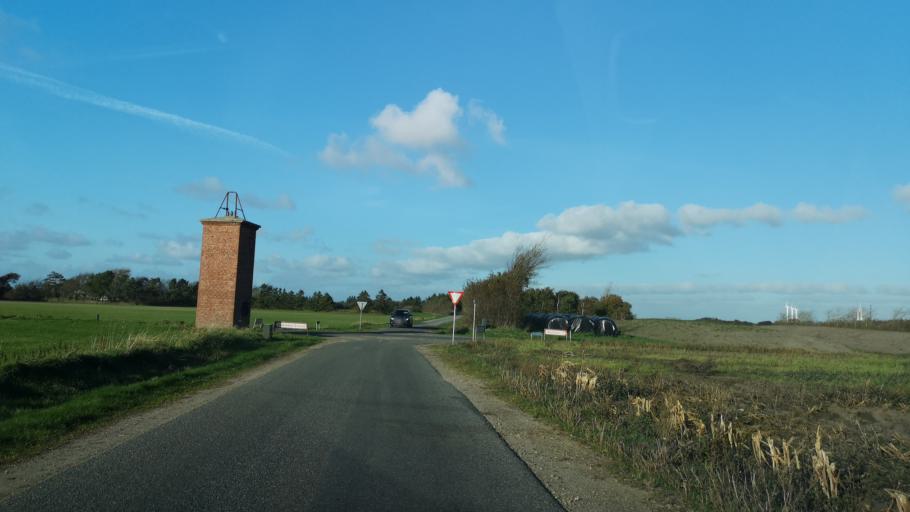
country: DK
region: Central Jutland
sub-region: Ringkobing-Skjern Kommune
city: Skjern
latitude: 55.8564
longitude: 8.3507
